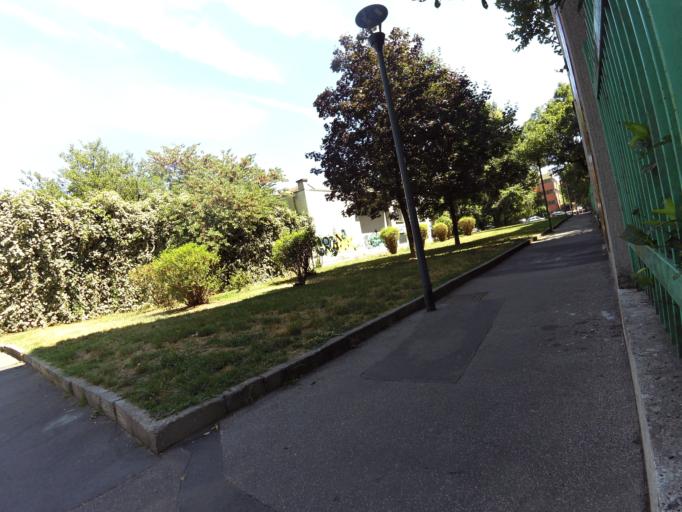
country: IT
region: Lombardy
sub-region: Citta metropolitana di Milano
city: Sesto San Giovanni
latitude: 45.4893
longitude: 9.2383
